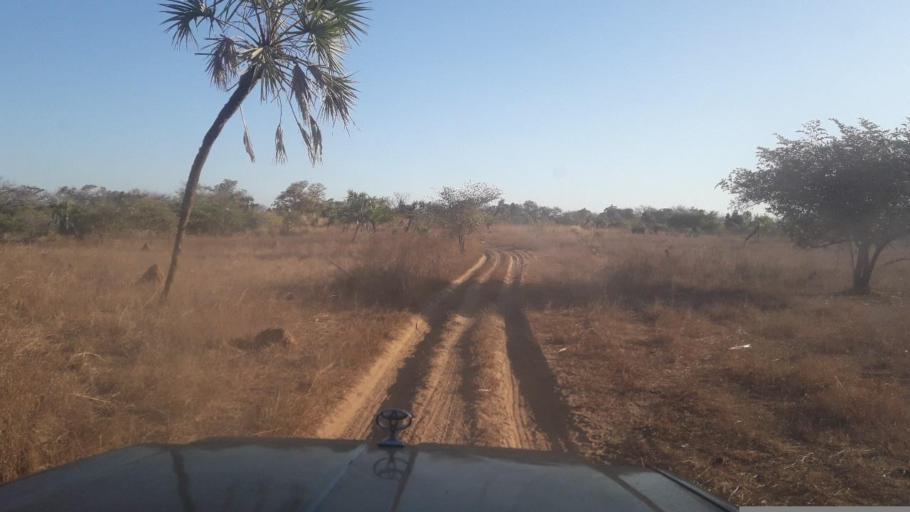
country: MG
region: Boeny
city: Sitampiky
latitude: -16.4996
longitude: 45.6040
